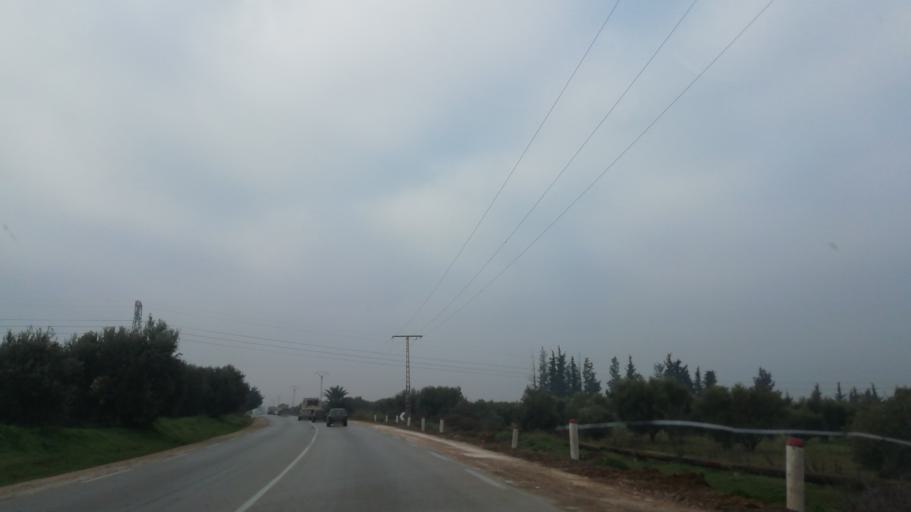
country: DZ
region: Relizane
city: Djidiouia
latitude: 35.9180
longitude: 0.7897
